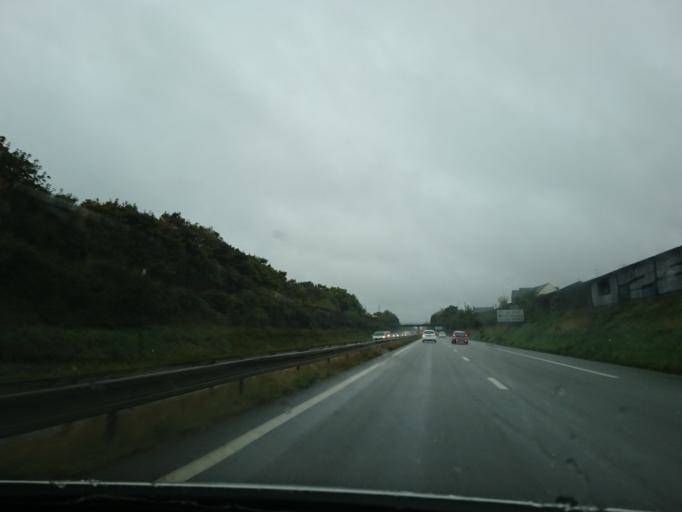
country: FR
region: Brittany
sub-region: Departement du Morbihan
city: Vannes
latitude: 47.6695
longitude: -2.7613
